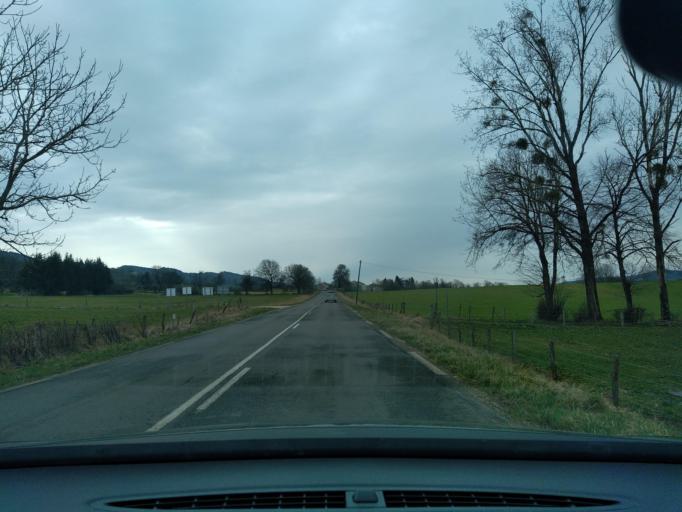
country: FR
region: Franche-Comte
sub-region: Departement du Jura
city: Arinthod
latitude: 46.3862
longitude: 5.5644
